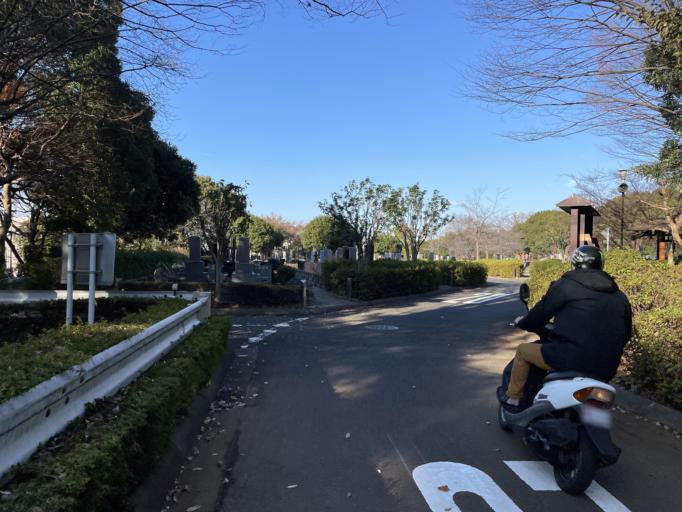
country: JP
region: Saitama
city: Asaka
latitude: 35.7839
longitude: 139.5811
